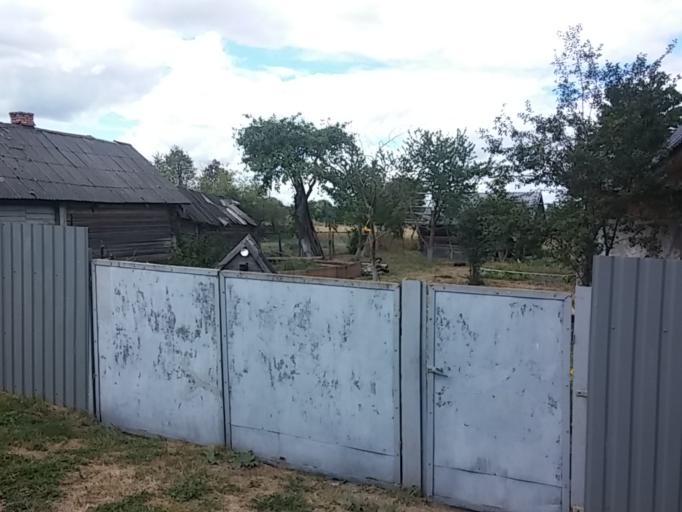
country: BY
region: Minsk
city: Chervyen'
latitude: 53.7803
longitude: 28.2687
